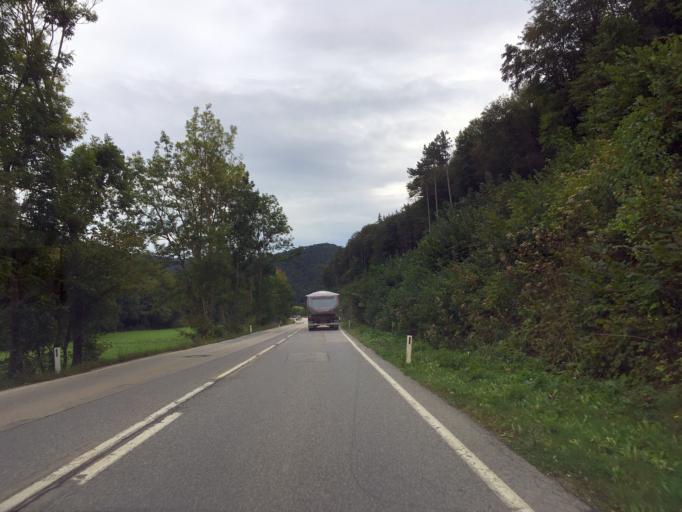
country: AT
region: Lower Austria
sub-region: Politischer Bezirk Modling
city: Giesshubl
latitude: 48.0723
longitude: 16.2219
